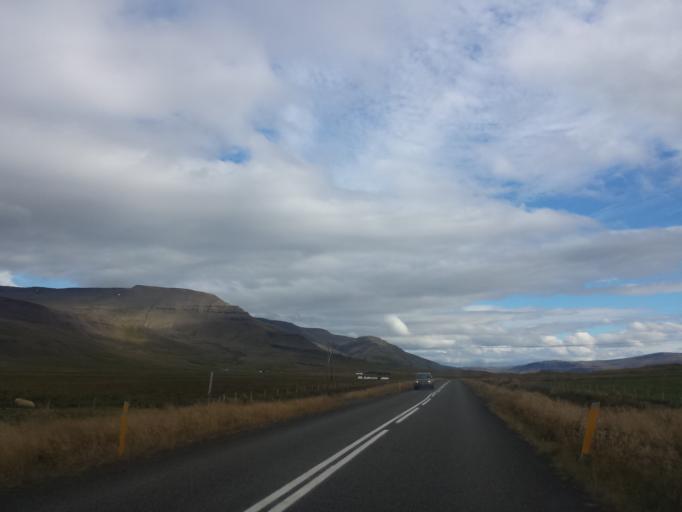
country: IS
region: West
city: Borgarnes
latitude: 64.4208
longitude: -21.7942
